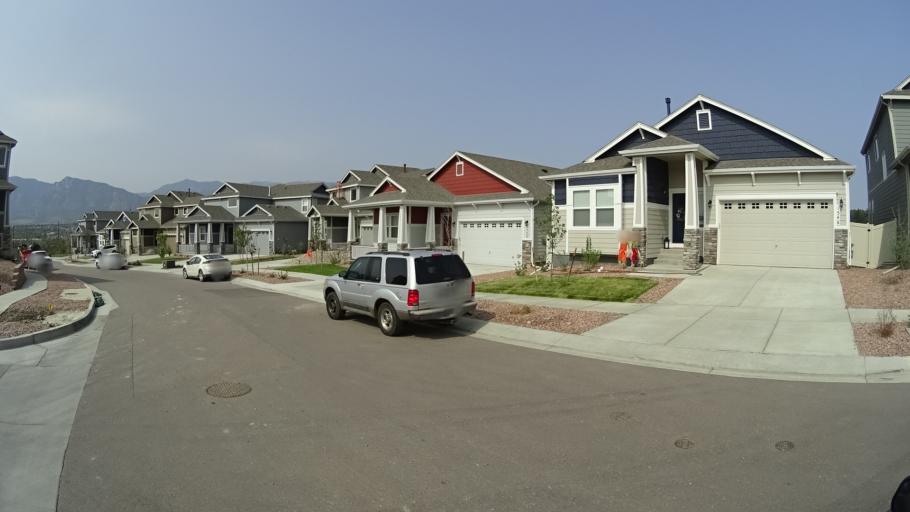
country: US
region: Colorado
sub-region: El Paso County
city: Stratmoor
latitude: 38.8096
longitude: -104.7917
